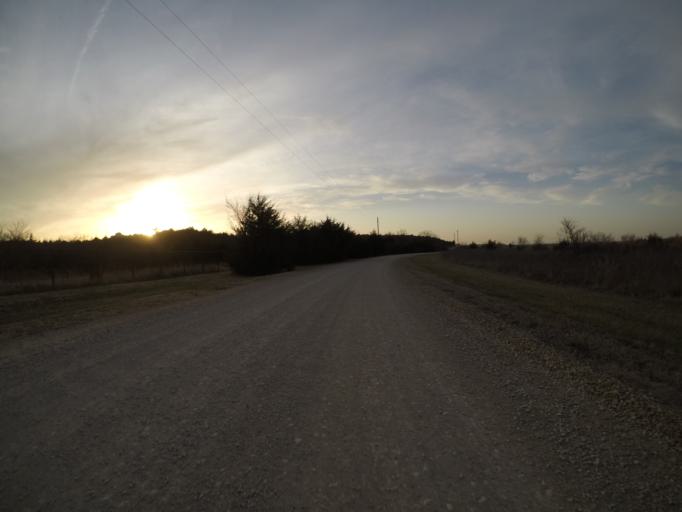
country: US
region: Kansas
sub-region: Riley County
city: Ogden
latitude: 39.1737
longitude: -96.6763
